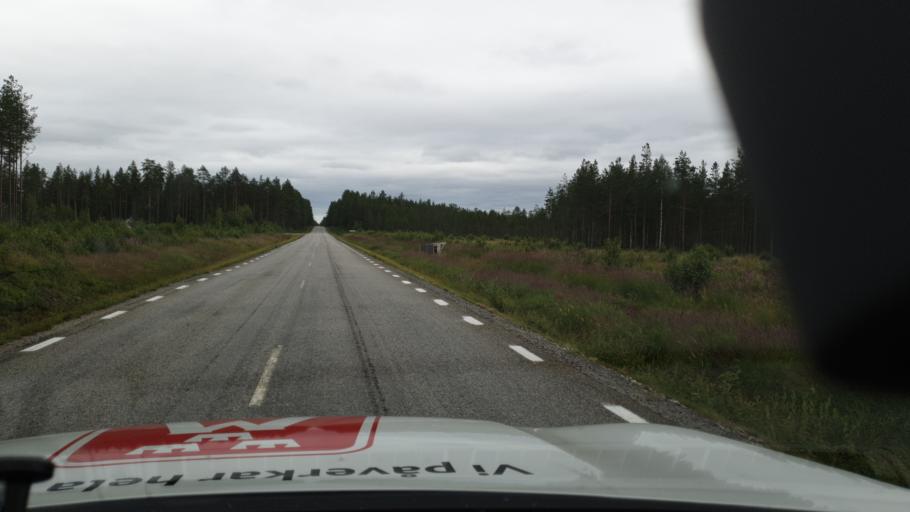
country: SE
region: Vaesterbotten
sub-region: Umea Kommun
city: Saevar
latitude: 64.0514
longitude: 20.4854
